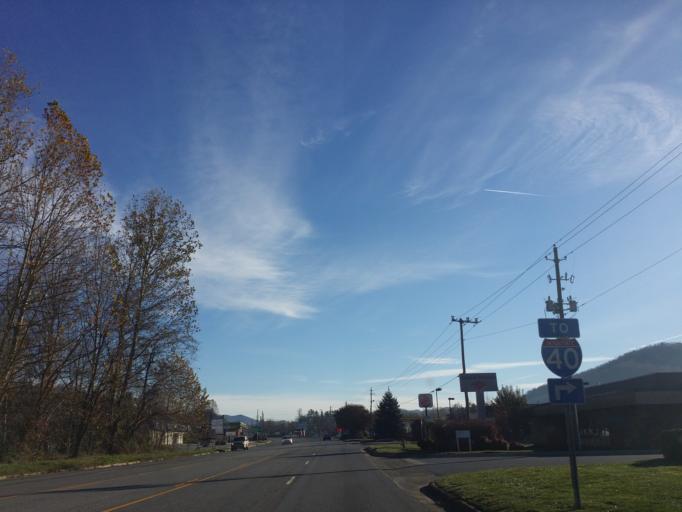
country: US
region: North Carolina
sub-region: Buncombe County
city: Swannanoa
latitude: 35.5995
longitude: -82.4060
